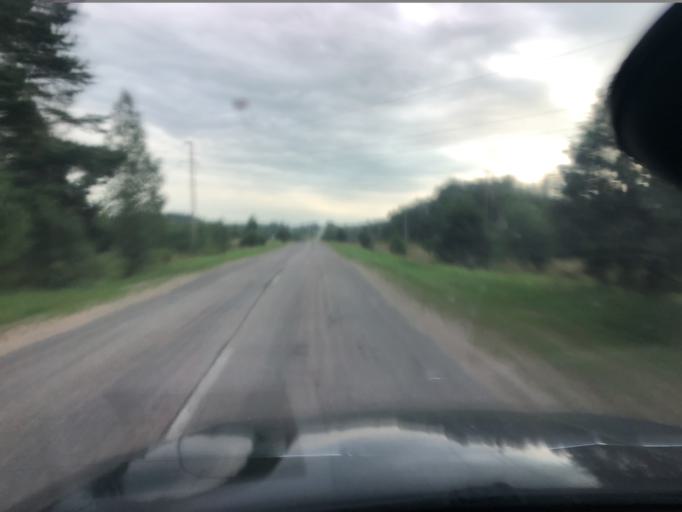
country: RU
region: Jaroslavl
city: Petrovsk
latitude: 57.0127
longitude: 38.9975
